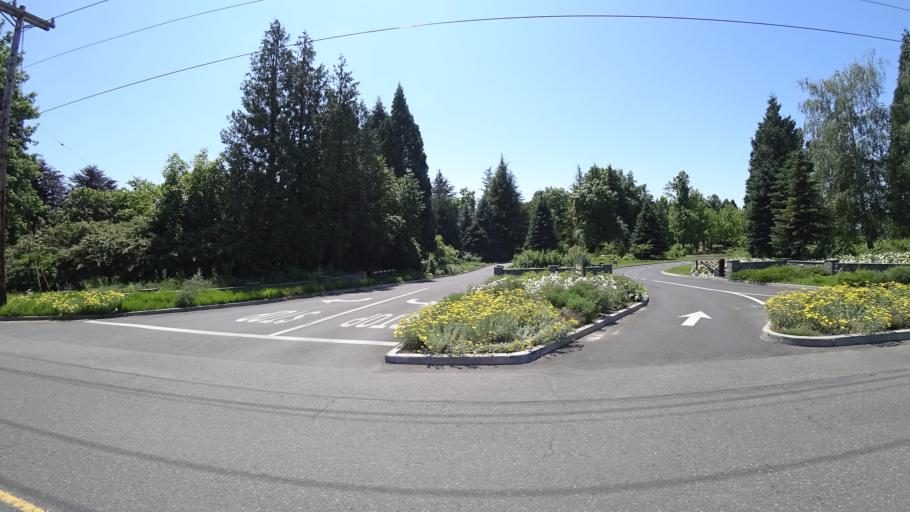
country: US
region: Oregon
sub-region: Multnomah County
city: Fairview
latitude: 45.5555
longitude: -122.4448
